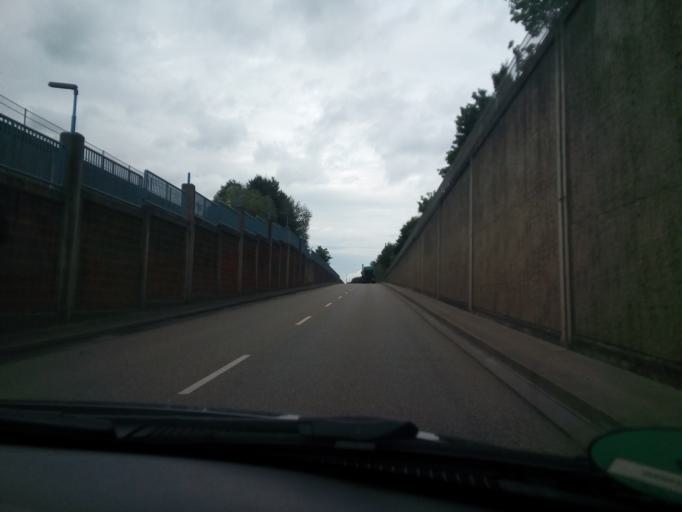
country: DE
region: Baden-Wuerttemberg
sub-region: Karlsruhe Region
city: Ottersweier
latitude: 48.6776
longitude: 8.1103
